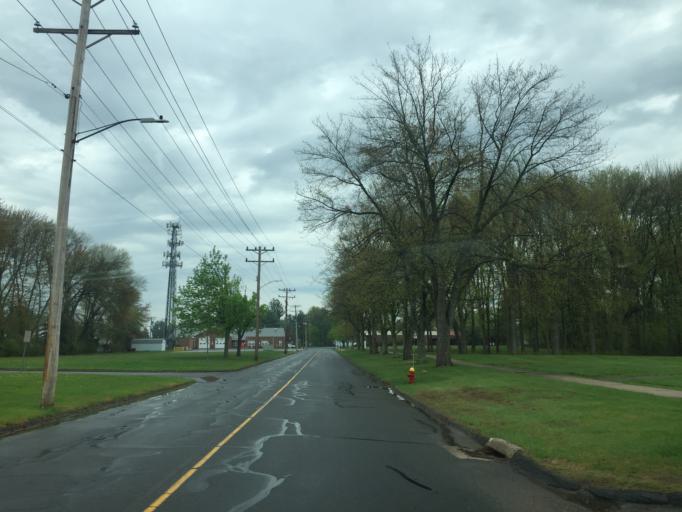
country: US
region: Connecticut
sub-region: Hartford County
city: Blue Hills
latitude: 41.8198
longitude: -72.6989
